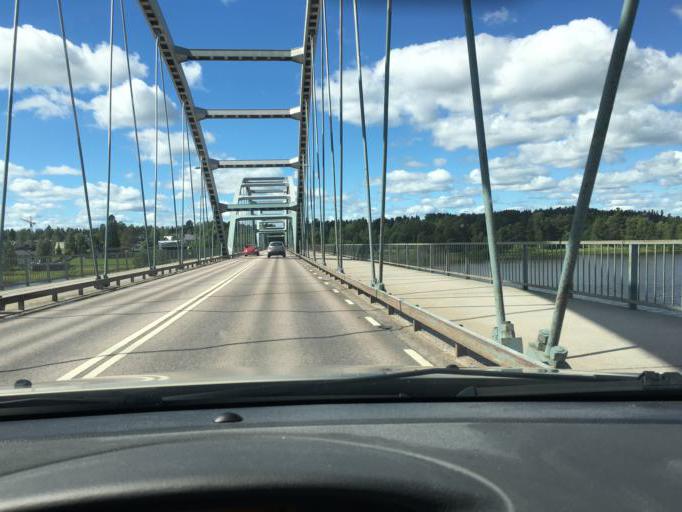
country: SE
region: Norrbotten
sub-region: Lulea Kommun
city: Bergnaset
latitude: 65.5787
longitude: 22.1210
